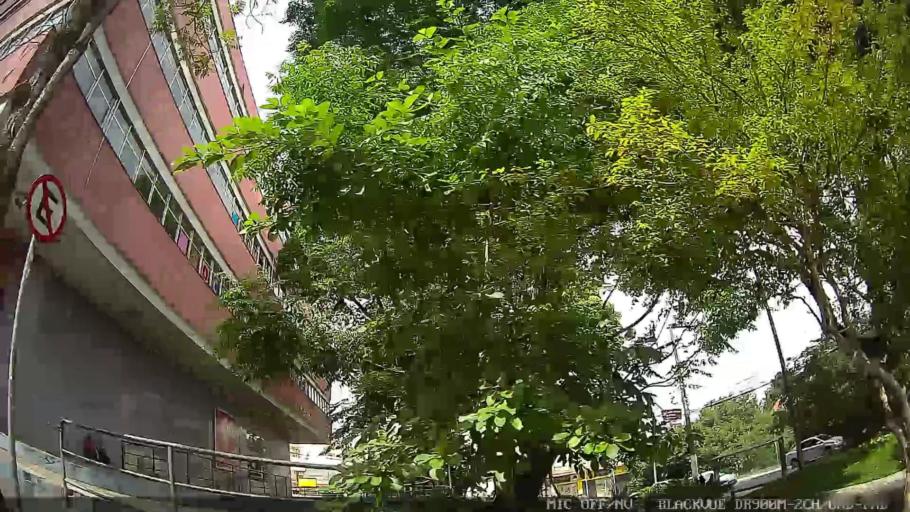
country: BR
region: Sao Paulo
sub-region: Guarulhos
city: Guarulhos
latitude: -23.5255
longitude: -46.5485
